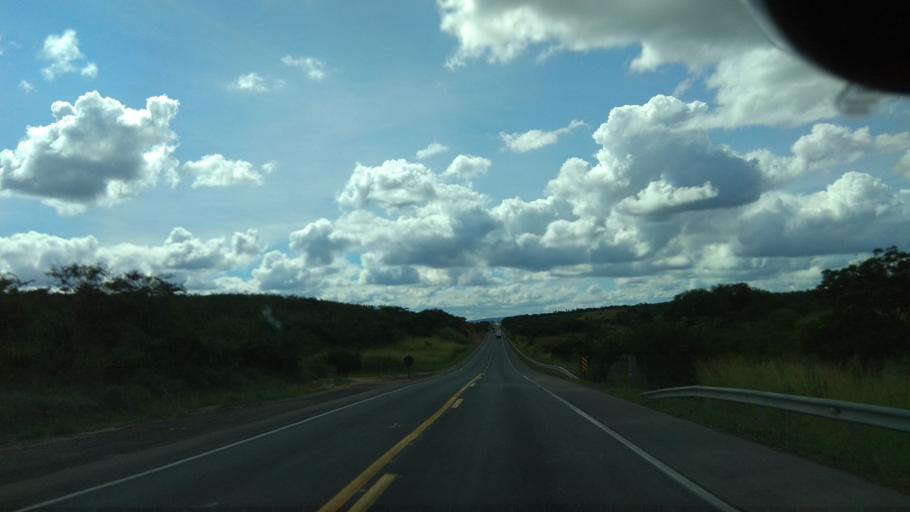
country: BR
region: Bahia
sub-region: Jaguaquara
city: Jaguaquara
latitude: -13.4514
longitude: -40.0318
